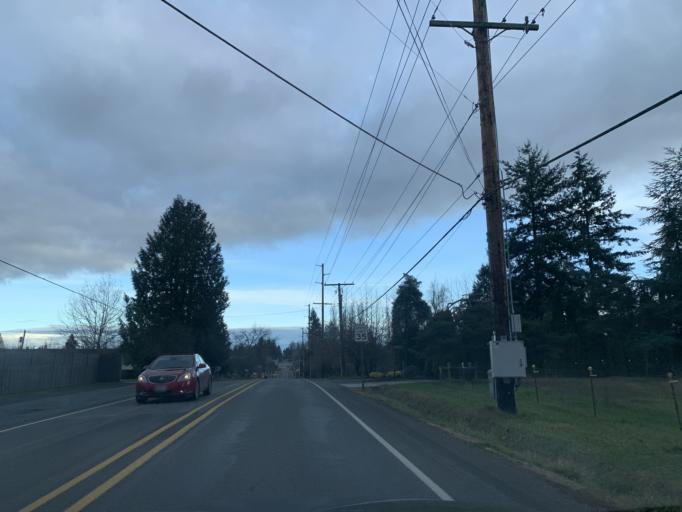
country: US
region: Washington
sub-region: Pierce County
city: Milton
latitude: 47.2355
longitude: -122.3038
